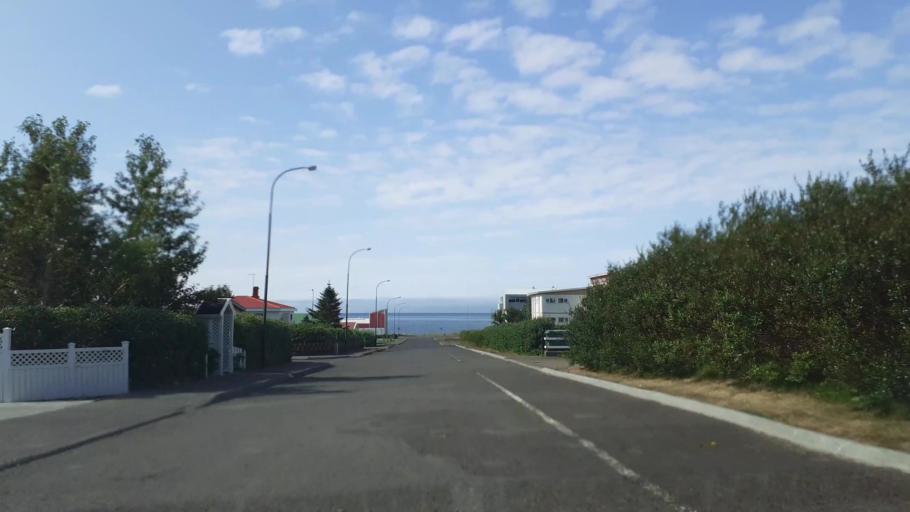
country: IS
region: Northwest
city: Saudarkrokur
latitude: 65.8225
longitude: -20.2995
